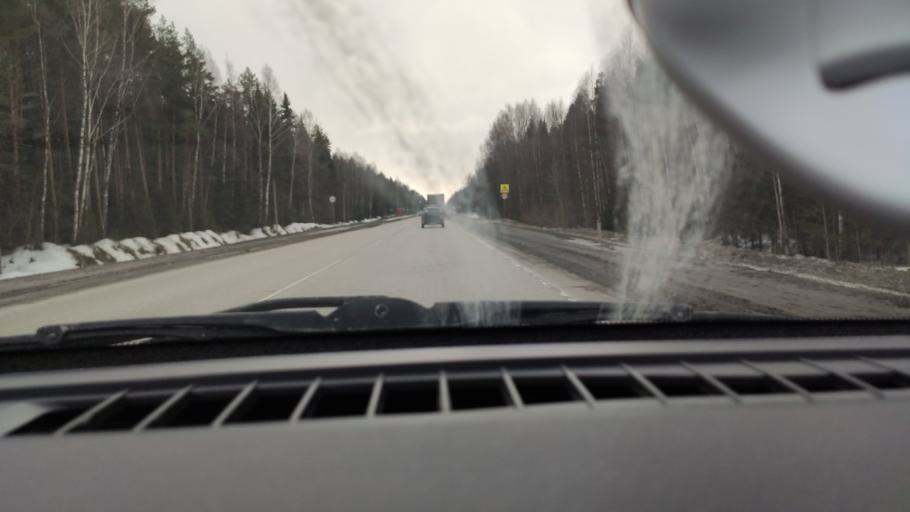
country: RU
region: Perm
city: Chaykovskaya
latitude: 58.0239
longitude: 55.5412
